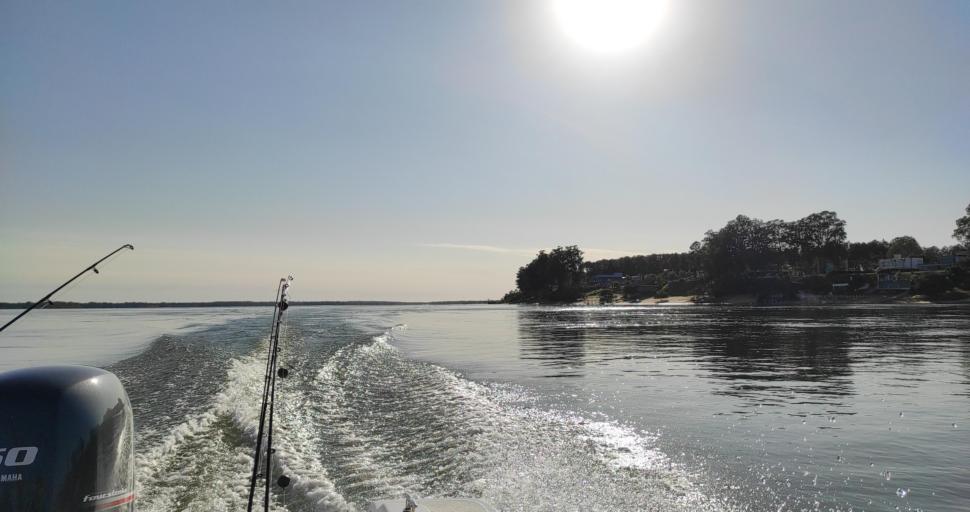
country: AR
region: Corrientes
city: Ituzaingo
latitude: -27.5999
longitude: -56.8180
